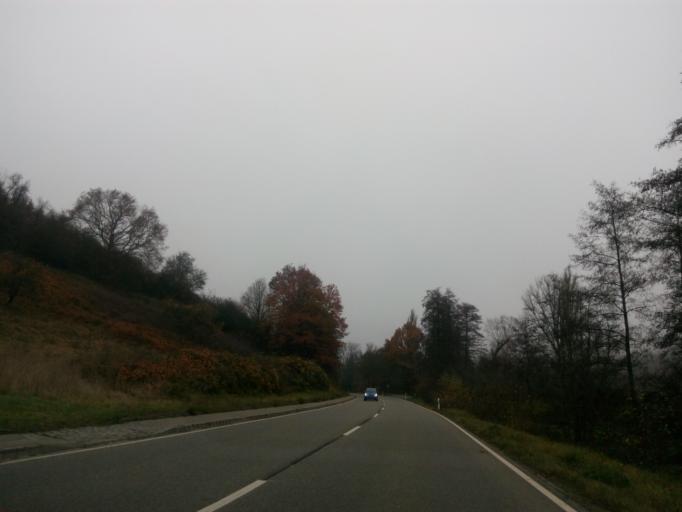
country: DE
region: Rheinland-Pfalz
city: Rutsweiler an der Lauter
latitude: 49.5719
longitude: 7.6213
